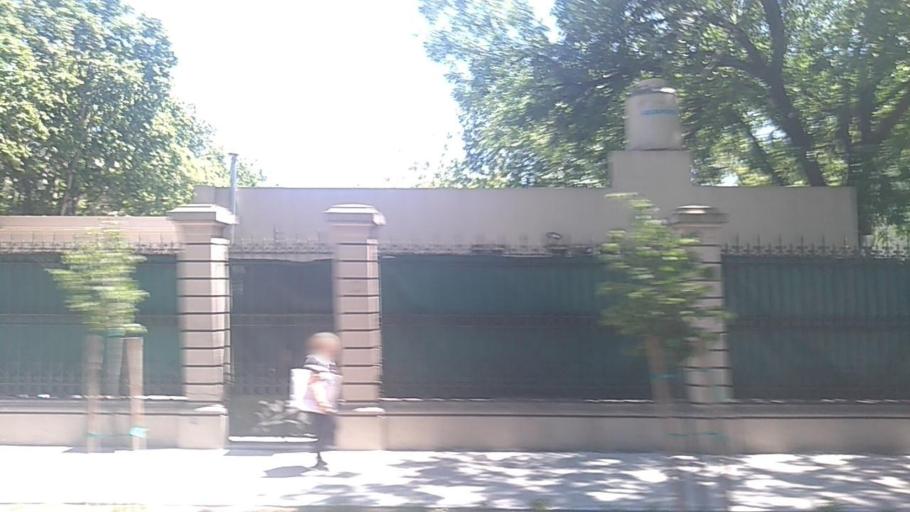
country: AR
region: Buenos Aires F.D.
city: Villa Santa Rita
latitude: -34.6048
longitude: -58.5102
